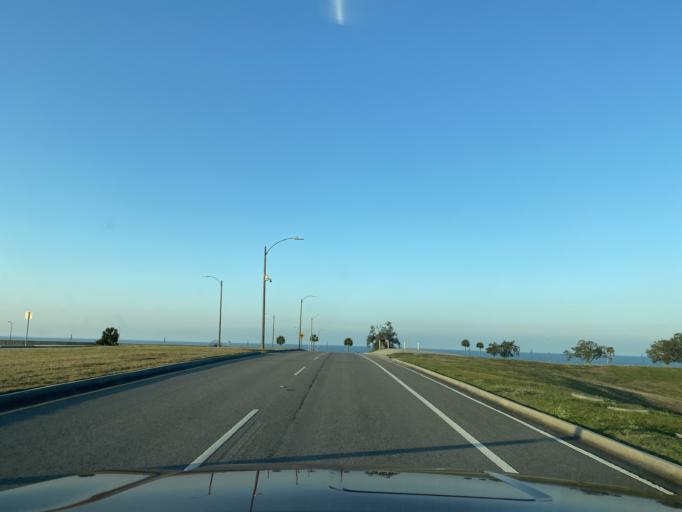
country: US
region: Louisiana
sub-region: Orleans Parish
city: New Orleans
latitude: 30.0325
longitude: -90.0526
